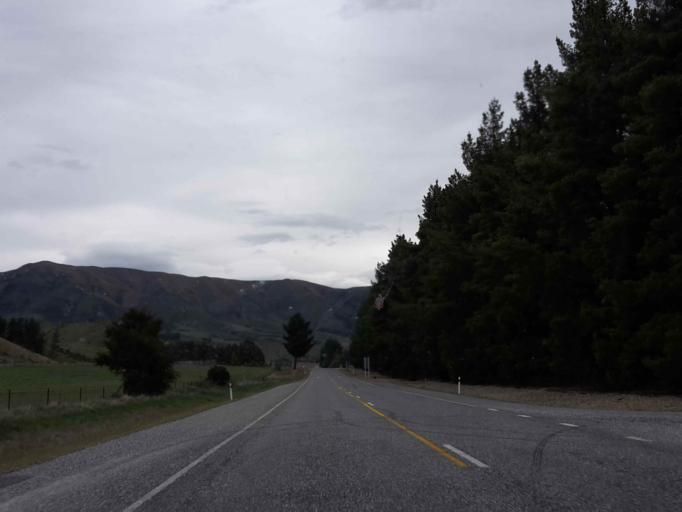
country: NZ
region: Otago
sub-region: Queenstown-Lakes District
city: Wanaka
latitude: -44.7334
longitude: 169.2907
